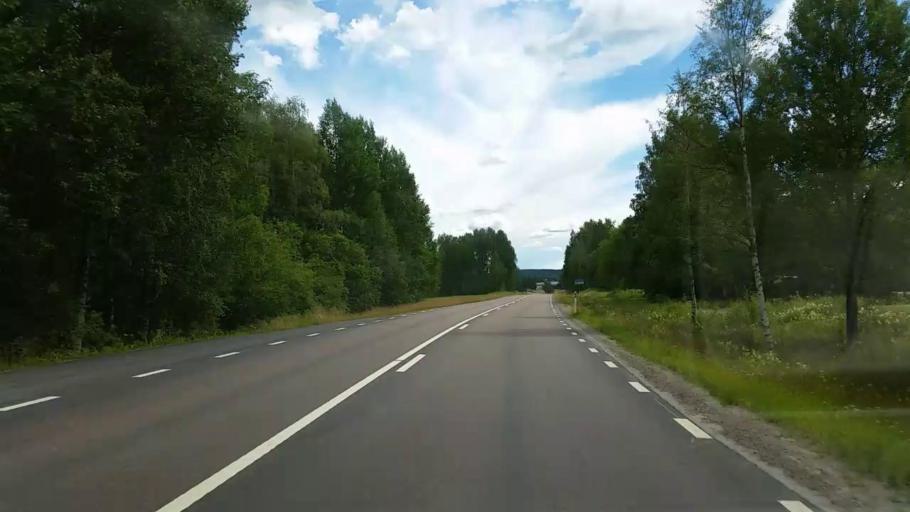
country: SE
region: Gaevleborg
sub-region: Ovanakers Kommun
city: Edsbyn
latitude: 61.3808
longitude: 15.8342
